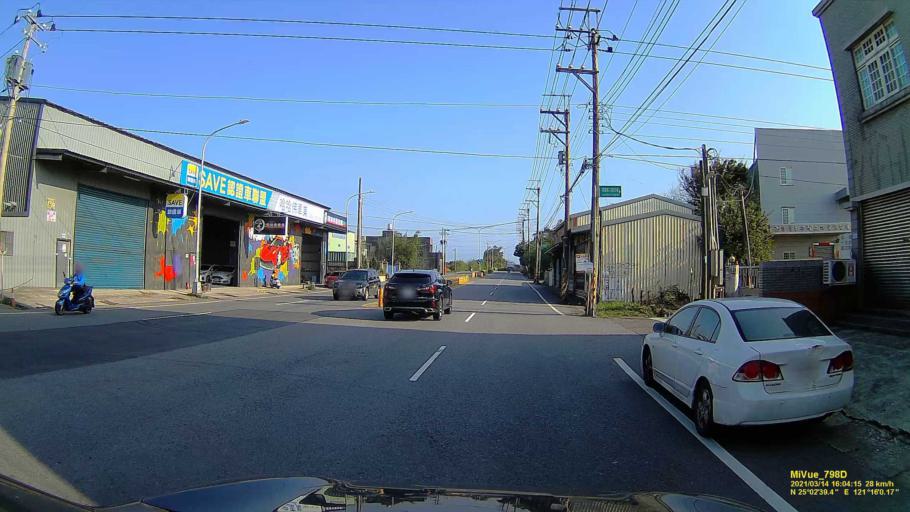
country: TW
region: Taiwan
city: Taoyuan City
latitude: 25.0442
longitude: 121.2668
